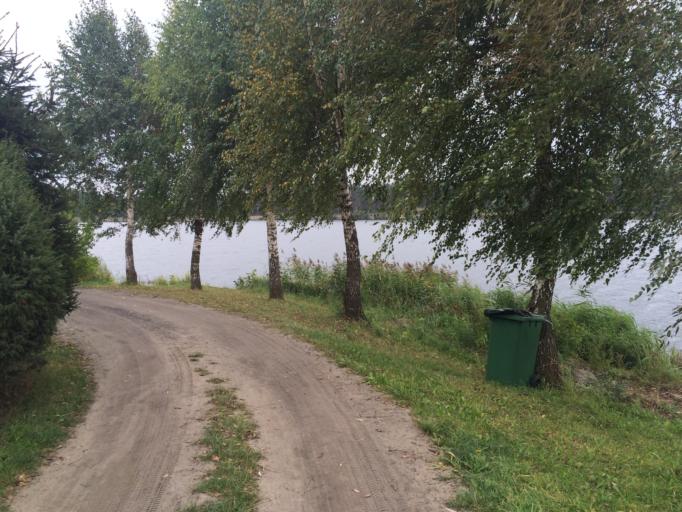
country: PL
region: Swietokrzyskie
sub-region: Powiat starachowicki
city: Starachowice
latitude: 51.0266
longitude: 21.0504
